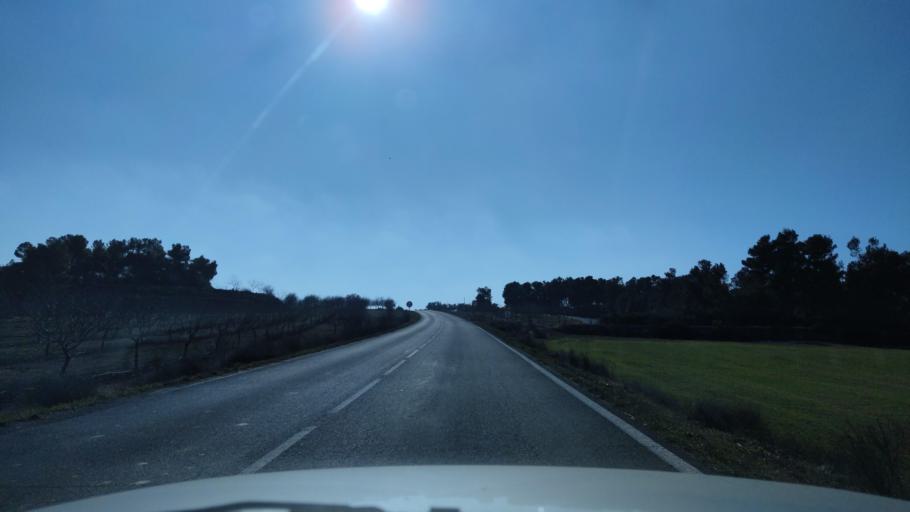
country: ES
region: Catalonia
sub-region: Provincia de Lleida
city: Maials
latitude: 41.3516
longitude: 0.4698
